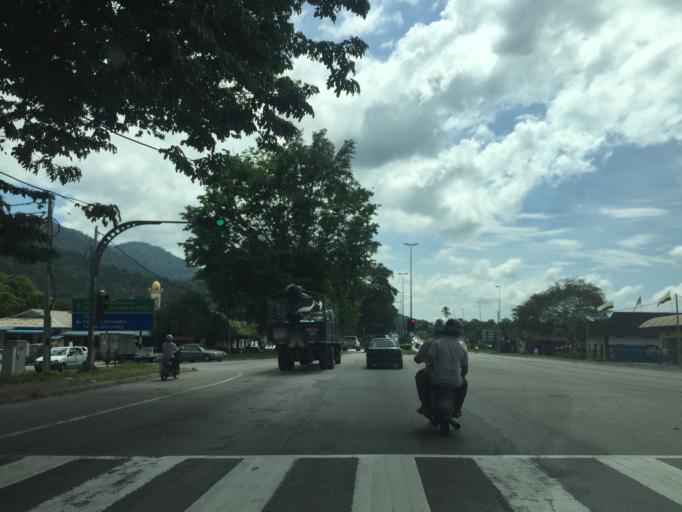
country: MY
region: Perak
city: Kampar
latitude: 4.3054
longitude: 101.1560
